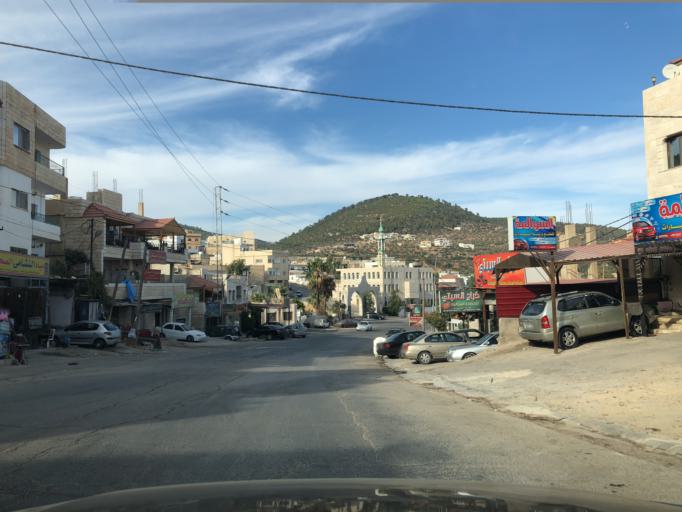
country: JO
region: Irbid
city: Sakib
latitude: 32.2824
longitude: 35.8114
